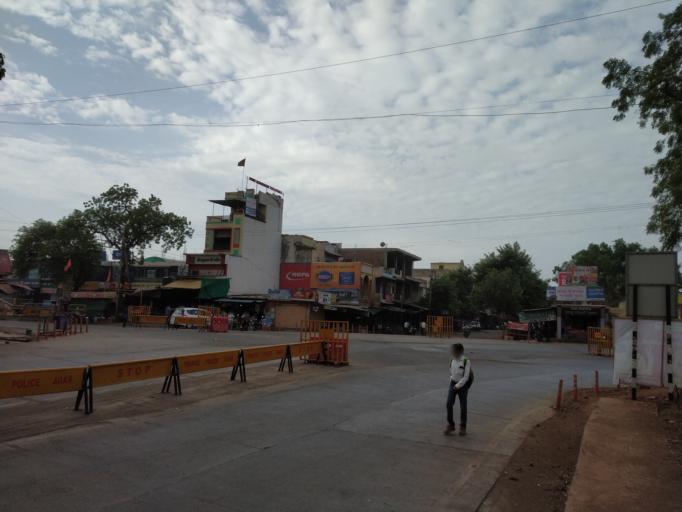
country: IN
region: Madhya Pradesh
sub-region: Shajapur
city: Agar
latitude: 23.7202
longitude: 76.0186
